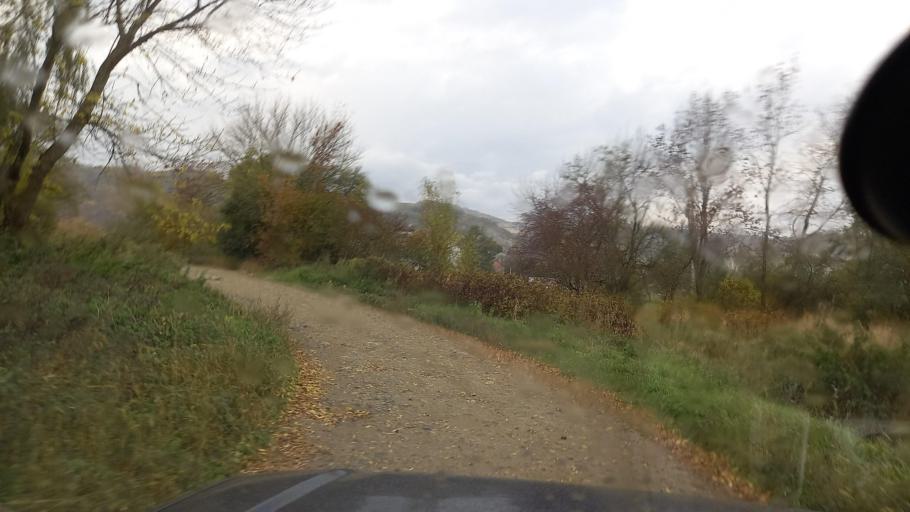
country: RU
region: Krasnodarskiy
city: Shedok
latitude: 44.1738
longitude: 40.8431
